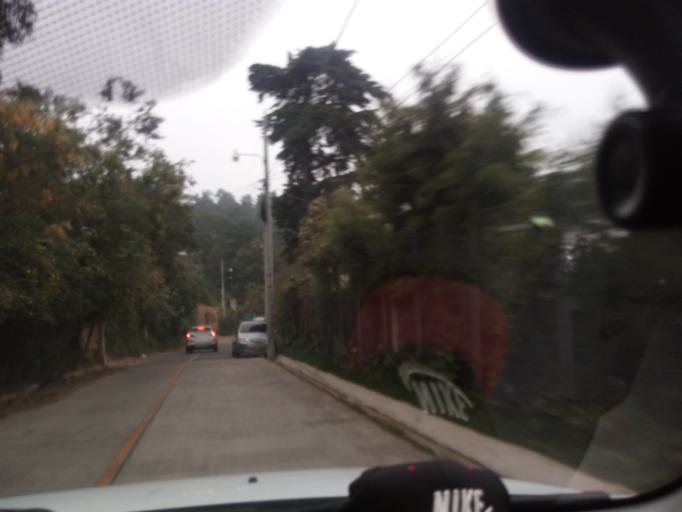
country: GT
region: Sacatepequez
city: Santa Lucia Milpas Altas
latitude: 14.5833
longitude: -90.7102
